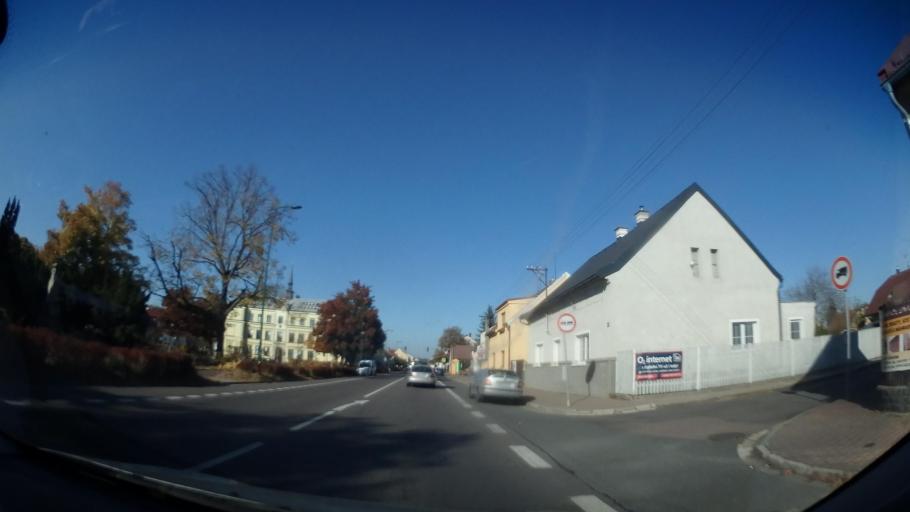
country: CZ
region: Pardubicky
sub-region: Okres Chrudim
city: Slatinany
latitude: 49.9163
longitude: 15.8159
